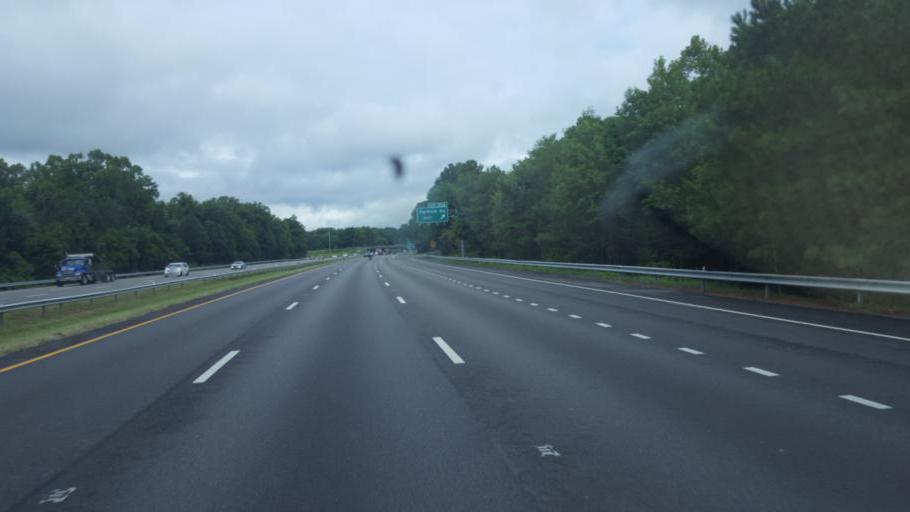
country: US
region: Virginia
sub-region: Henrico County
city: Chamberlayne
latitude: 37.6309
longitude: -77.4495
